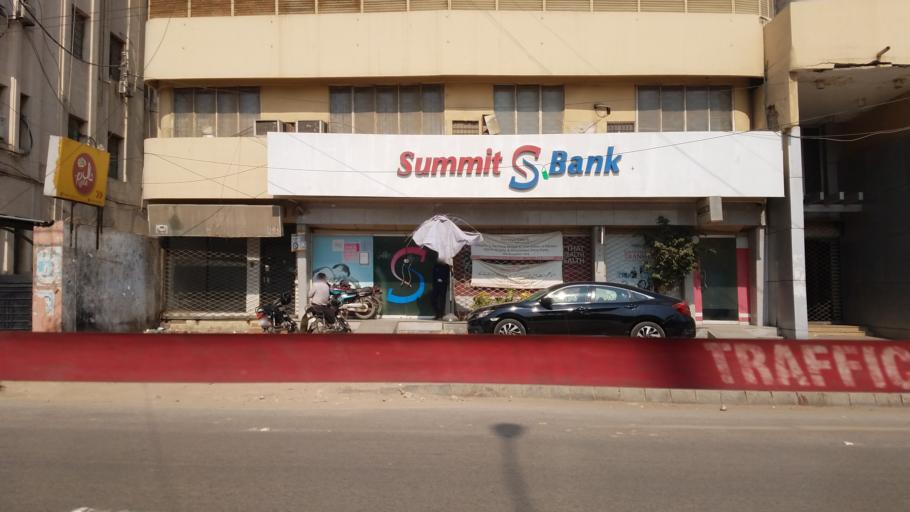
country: PK
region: Sindh
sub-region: Karachi District
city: Karachi
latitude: 24.8497
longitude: 67.0068
